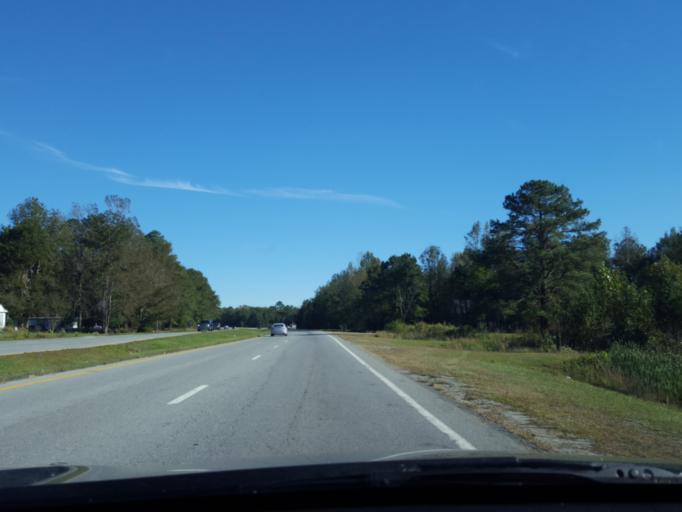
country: US
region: North Carolina
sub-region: Beaufort County
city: Washington
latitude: 35.6095
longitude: -77.1529
